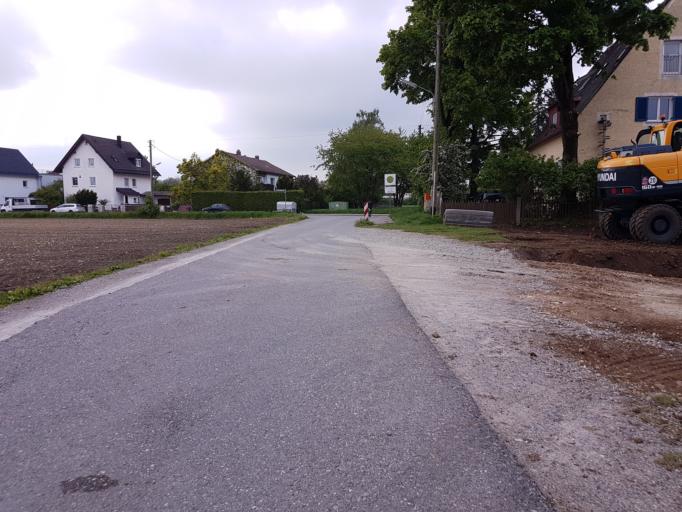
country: DE
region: Bavaria
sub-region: Upper Bavaria
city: Karlsfeld
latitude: 48.1832
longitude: 11.4558
